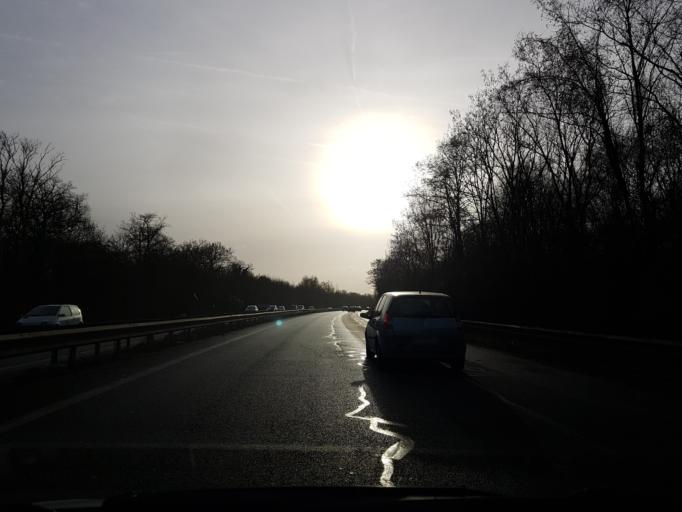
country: FR
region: Ile-de-France
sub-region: Departement de Seine-et-Marne
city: Lieusaint
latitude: 48.6491
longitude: 2.5313
